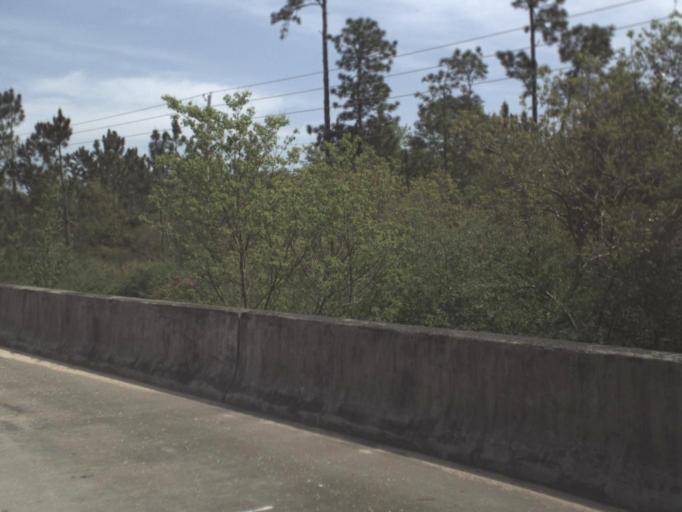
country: US
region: Florida
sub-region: Escambia County
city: Gonzalez
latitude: 30.5348
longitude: -87.3431
